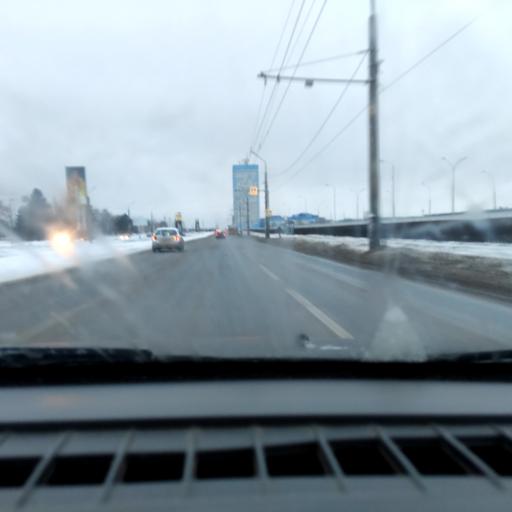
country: RU
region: Samara
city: Tol'yatti
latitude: 53.5545
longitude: 49.2767
